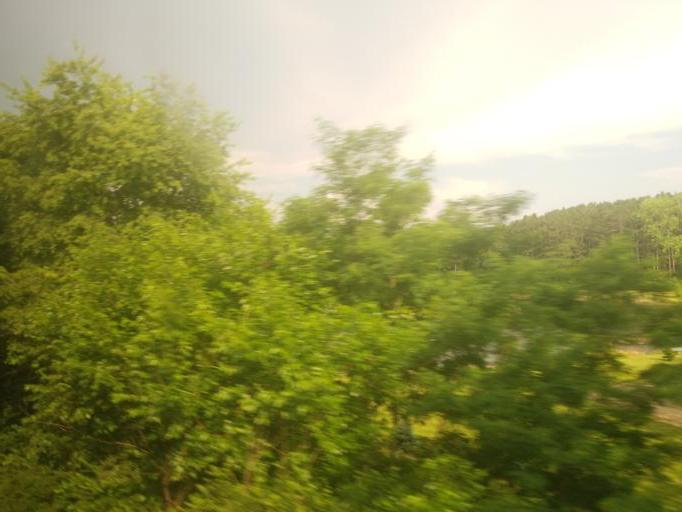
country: US
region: Illinois
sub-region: Bureau County
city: Princeton
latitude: 41.3486
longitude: -89.6189
